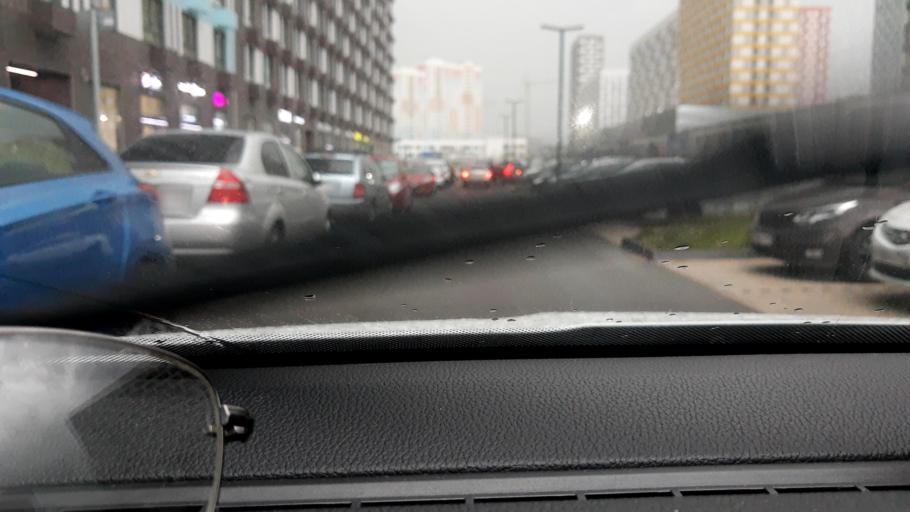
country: RU
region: Moskovskaya
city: Mytishchi
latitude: 55.9160
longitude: 37.7217
